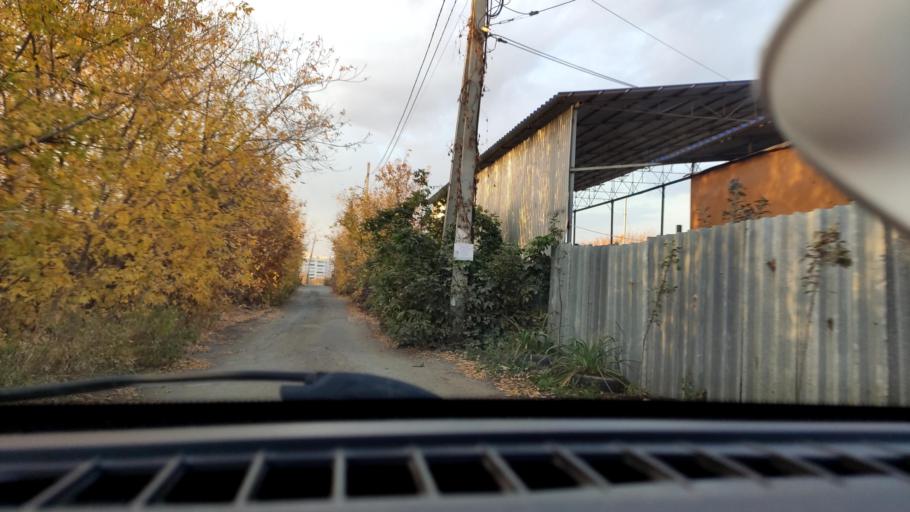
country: RU
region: Samara
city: Samara
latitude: 53.2726
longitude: 50.2287
